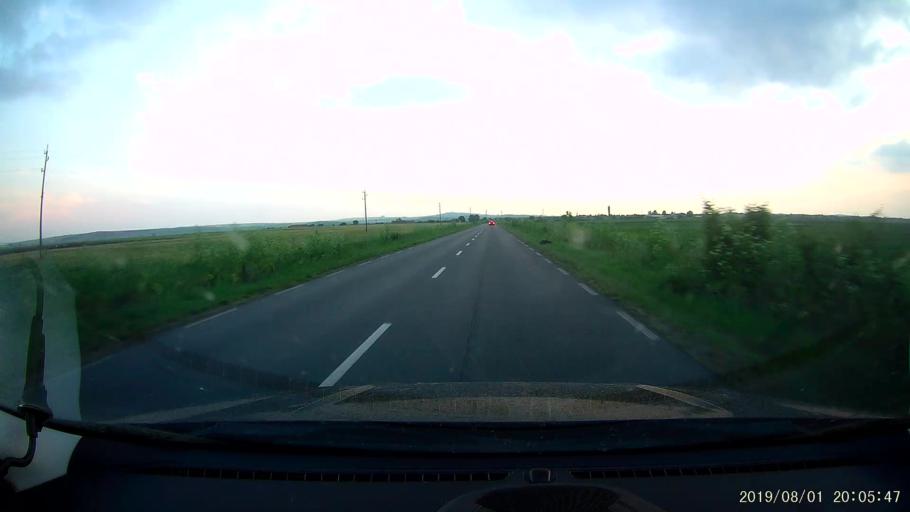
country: BG
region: Yambol
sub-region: Obshtina Yambol
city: Yambol
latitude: 42.5410
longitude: 26.5617
